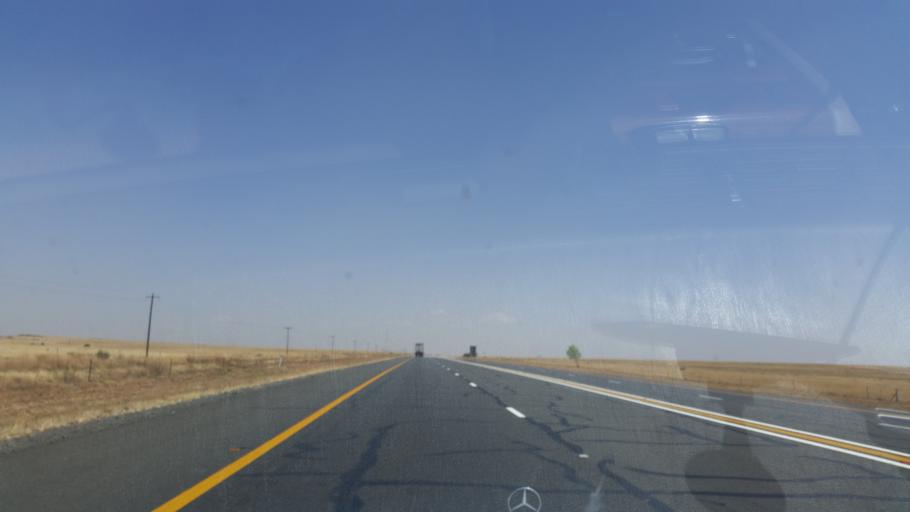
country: ZA
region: Orange Free State
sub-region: Lejweleputswa District Municipality
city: Brandfort
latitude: -28.8546
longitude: 26.5643
